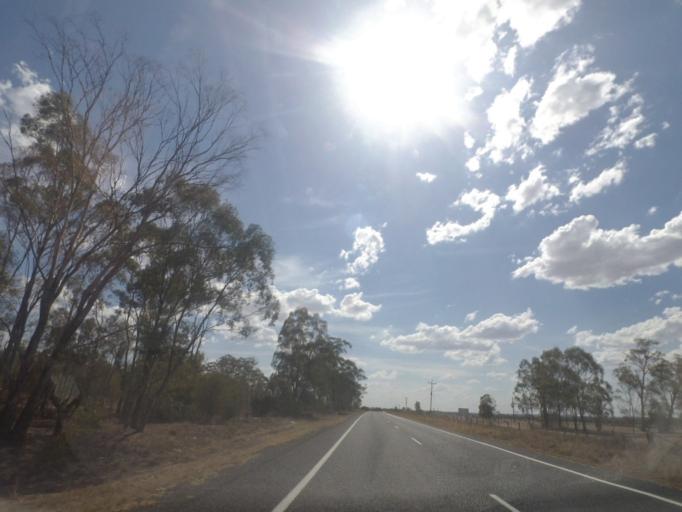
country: AU
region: New South Wales
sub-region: Moree Plains
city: Boggabilla
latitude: -28.4145
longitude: 151.1451
